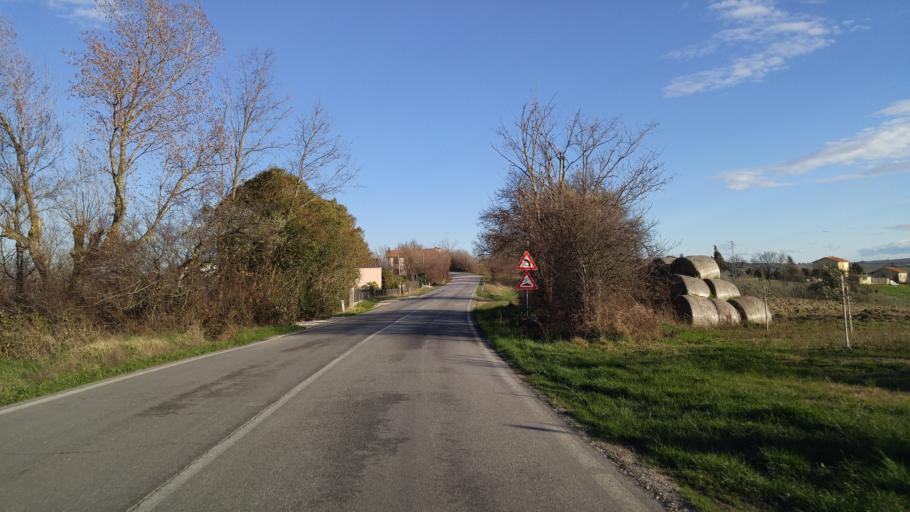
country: IT
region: The Marches
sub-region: Provincia di Pesaro e Urbino
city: Piagge
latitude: 43.7523
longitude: 12.9975
